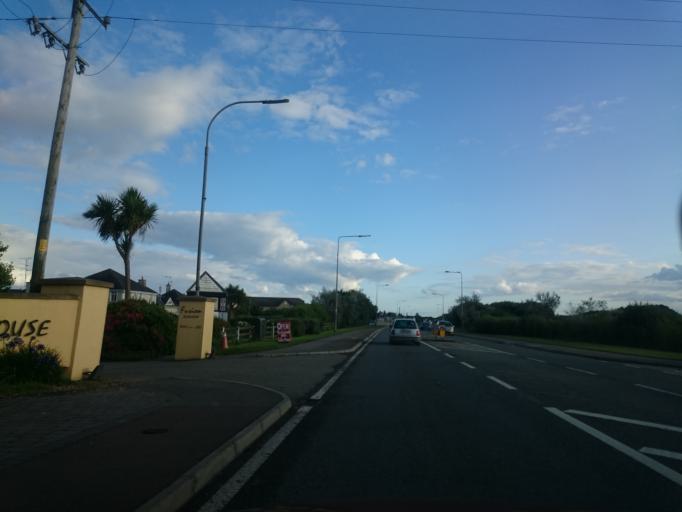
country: IE
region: Leinster
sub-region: Loch Garman
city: Ballygerry
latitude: 52.2495
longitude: -6.3440
